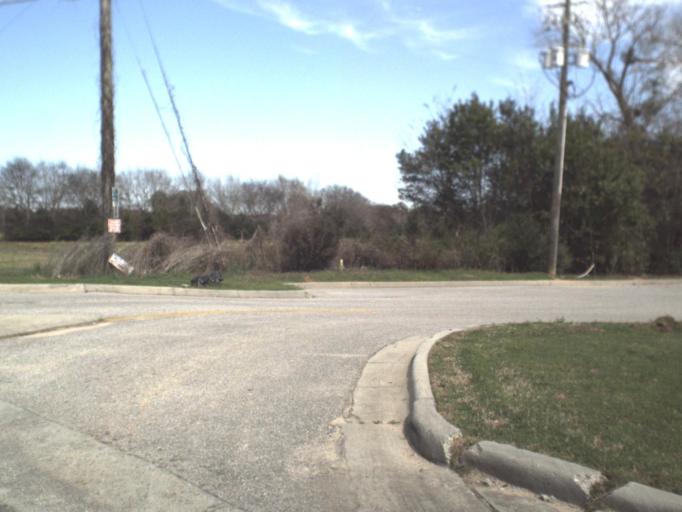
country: US
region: Florida
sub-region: Jackson County
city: Marianna
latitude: 30.8072
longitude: -85.3767
